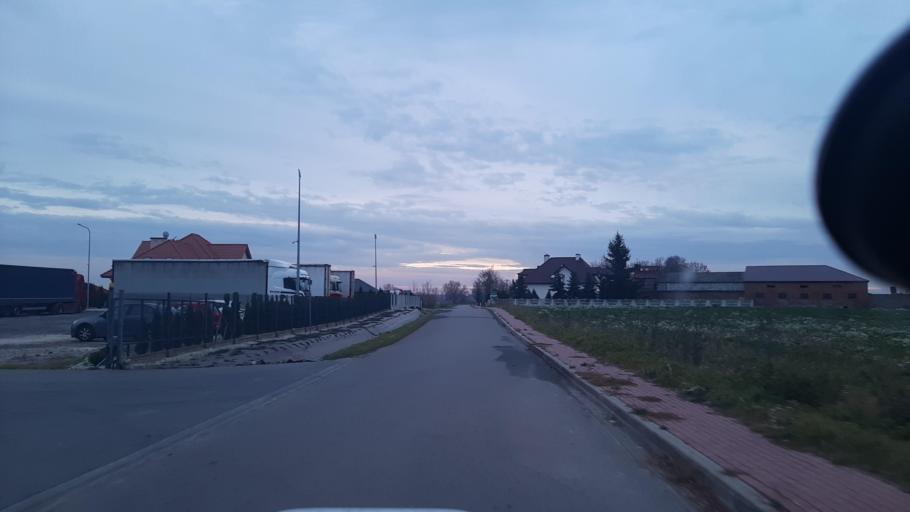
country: PL
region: Lublin Voivodeship
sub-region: Powiat lubelski
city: Garbow
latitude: 51.3686
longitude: 22.3850
